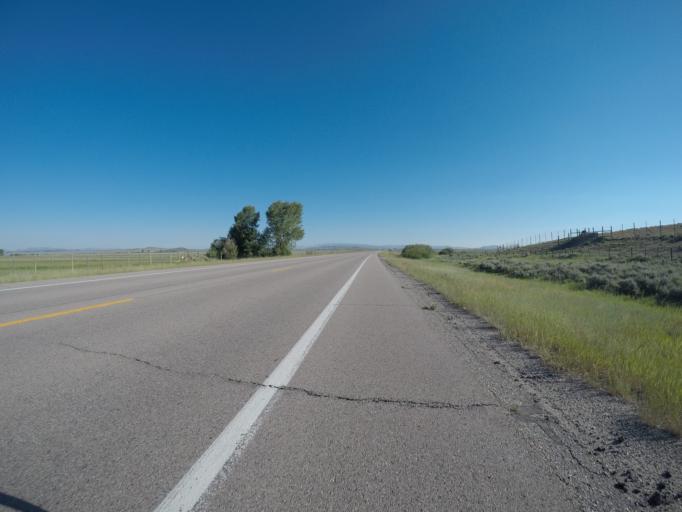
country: US
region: Wyoming
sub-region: Sublette County
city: Pinedale
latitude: 42.9517
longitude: -110.0863
